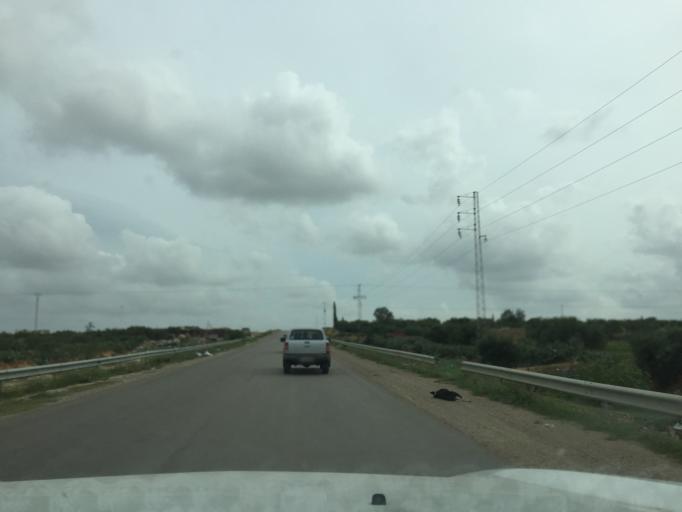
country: TN
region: Al Munastir
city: Jammal
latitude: 35.6062
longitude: 10.7646
